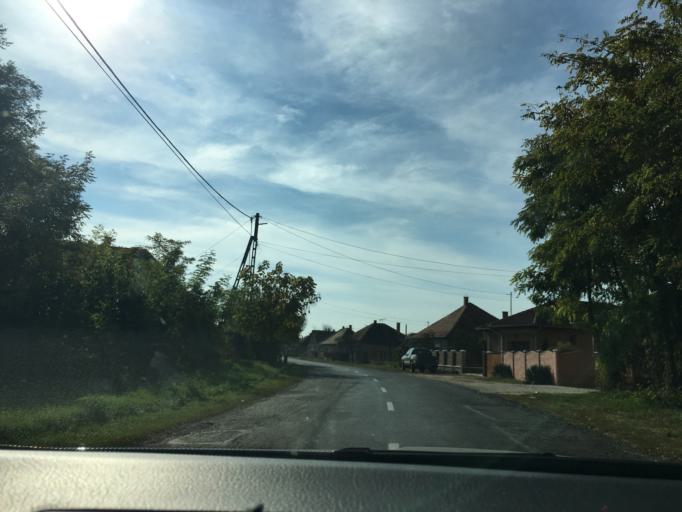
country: HU
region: Hajdu-Bihar
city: Nyirabrany
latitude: 47.5387
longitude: 22.0054
